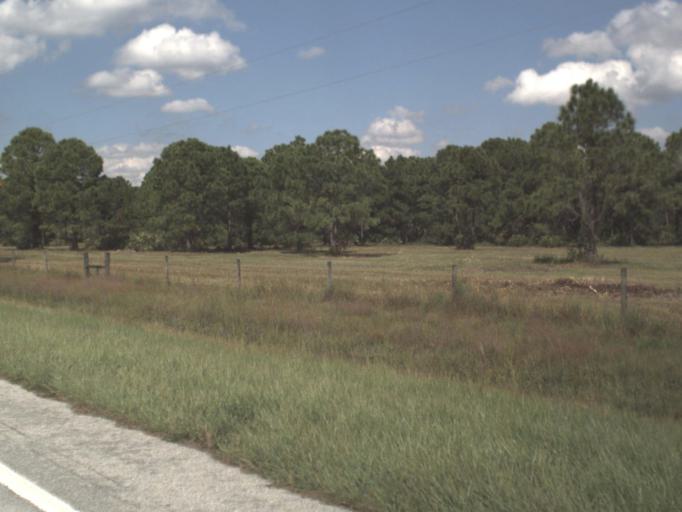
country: US
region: Florida
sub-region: Okeechobee County
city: Okeechobee
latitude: 27.3709
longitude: -81.0803
